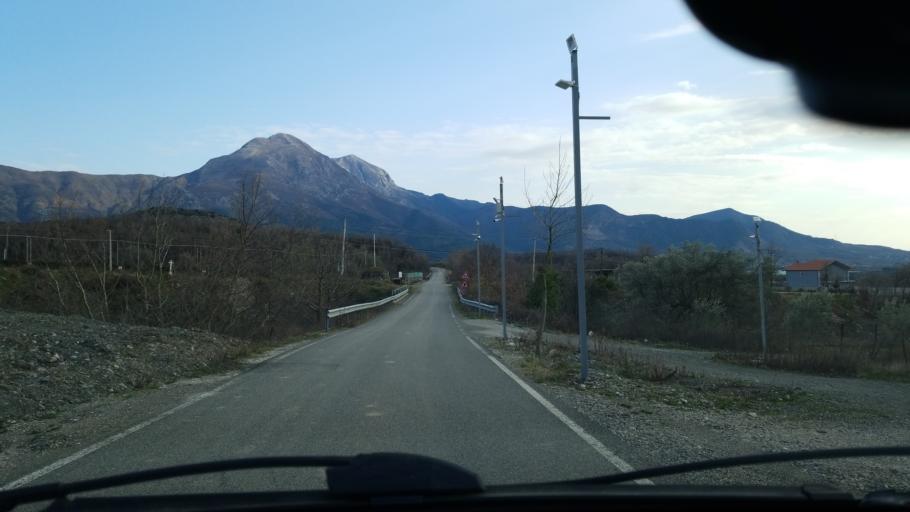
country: AL
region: Lezhe
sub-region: Rrethi i Lezhes
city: Kallmeti i Madh
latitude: 41.8814
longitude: 19.6920
